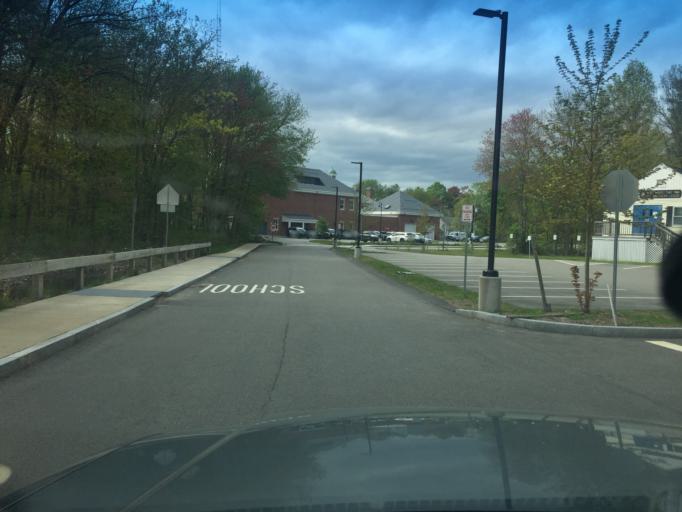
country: US
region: Massachusetts
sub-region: Norfolk County
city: Westwood
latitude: 42.2272
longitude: -71.2197
